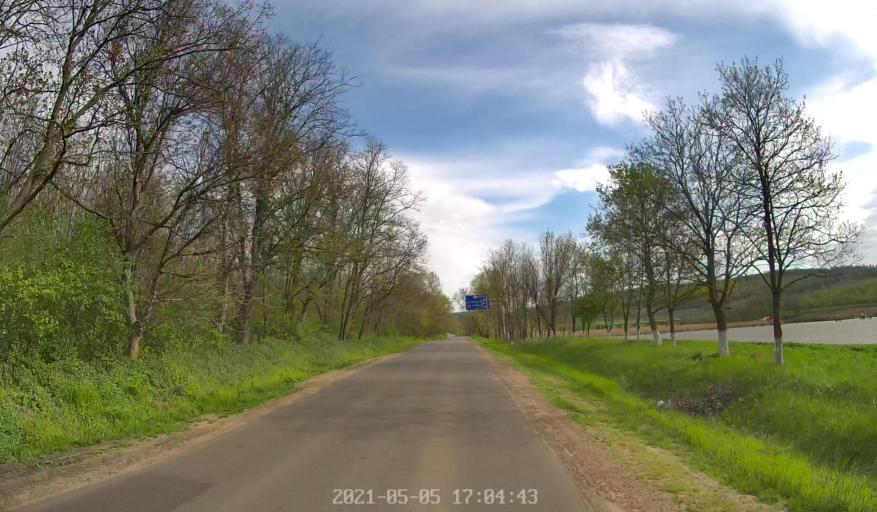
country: MD
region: Chisinau
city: Vadul lui Voda
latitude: 47.0378
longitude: 29.1364
